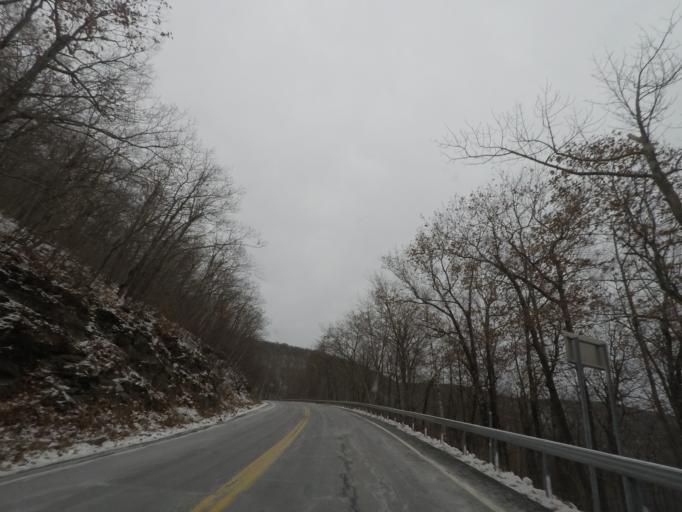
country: US
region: Massachusetts
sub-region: Berkshire County
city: Williamstown
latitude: 42.7301
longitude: -73.2753
